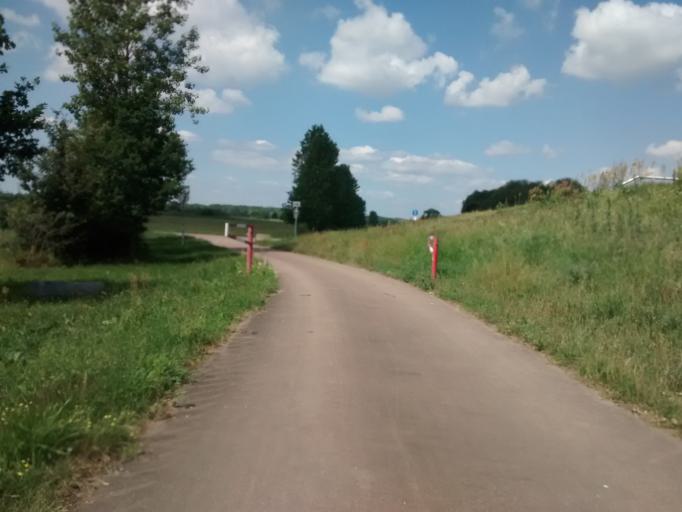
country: DE
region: Saxony-Anhalt
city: Bergwitz
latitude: 51.8539
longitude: 12.5514
